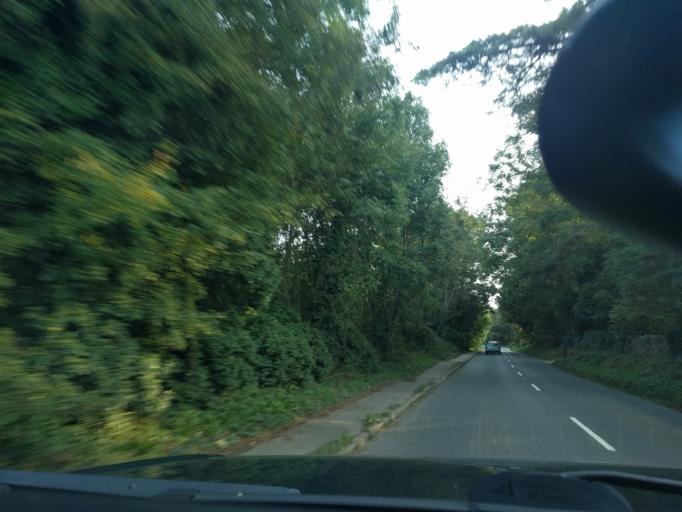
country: GB
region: England
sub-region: Wiltshire
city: Box
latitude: 51.4215
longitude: -2.2261
